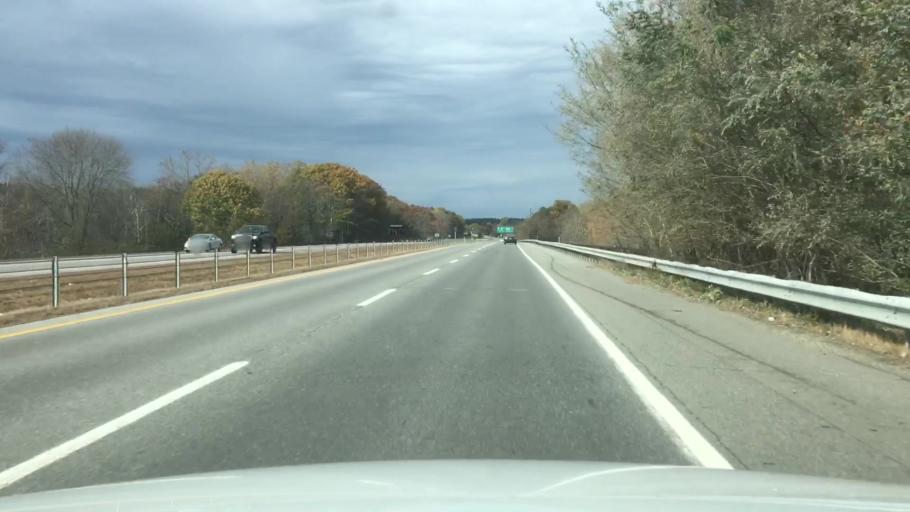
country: US
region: Maine
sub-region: Cumberland County
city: Brunswick
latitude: 43.9141
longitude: -69.9415
